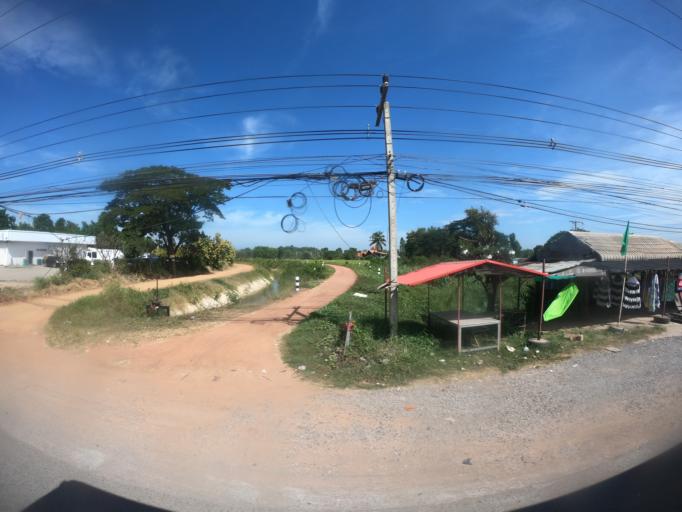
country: TH
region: Khon Kaen
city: Khon Kaen
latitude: 16.4379
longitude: 102.9367
